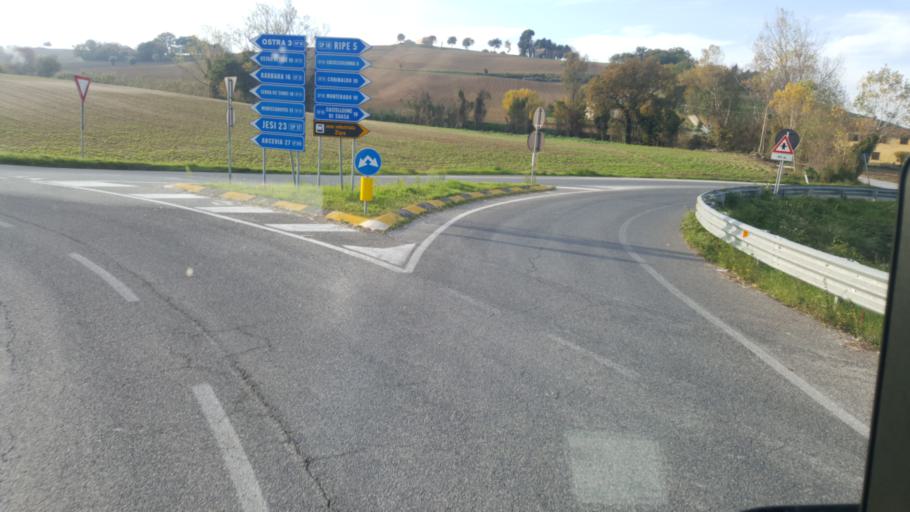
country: IT
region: The Marches
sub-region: Provincia di Ancona
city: Casine
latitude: 43.6419
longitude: 13.1396
